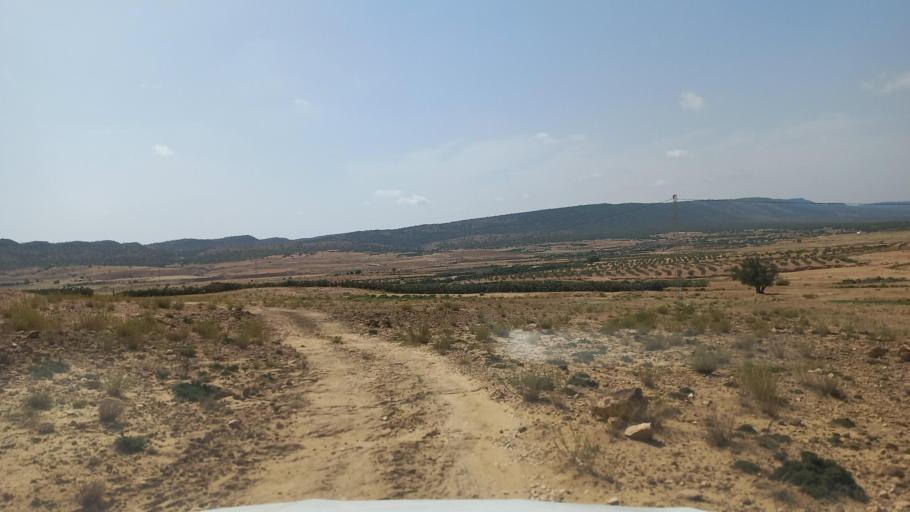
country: TN
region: Al Qasrayn
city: Sbiba
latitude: 35.3986
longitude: 8.9738
